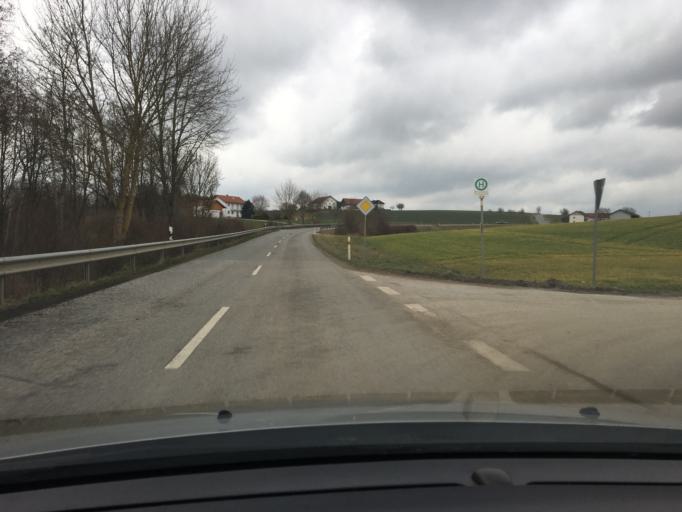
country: DE
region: Bavaria
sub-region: Lower Bavaria
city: Gangkofen
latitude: 48.4417
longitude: 12.5825
